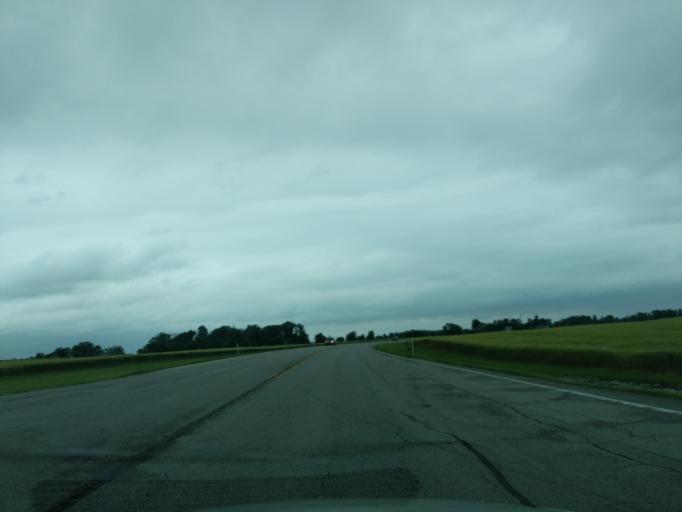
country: US
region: Indiana
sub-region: Hamilton County
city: Arcadia
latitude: 40.1866
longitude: -86.0207
